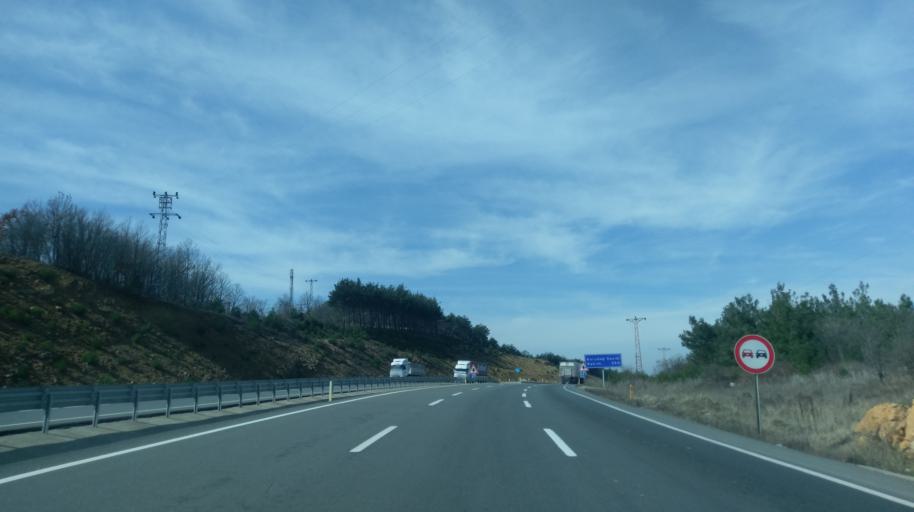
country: TR
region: Canakkale
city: Evrese
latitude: 40.7082
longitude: 26.7715
